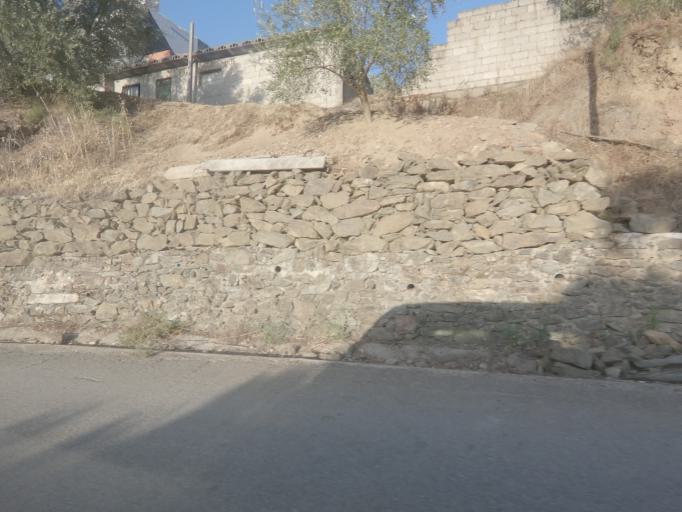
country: PT
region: Viseu
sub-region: Armamar
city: Armamar
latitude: 41.1466
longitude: -7.6788
